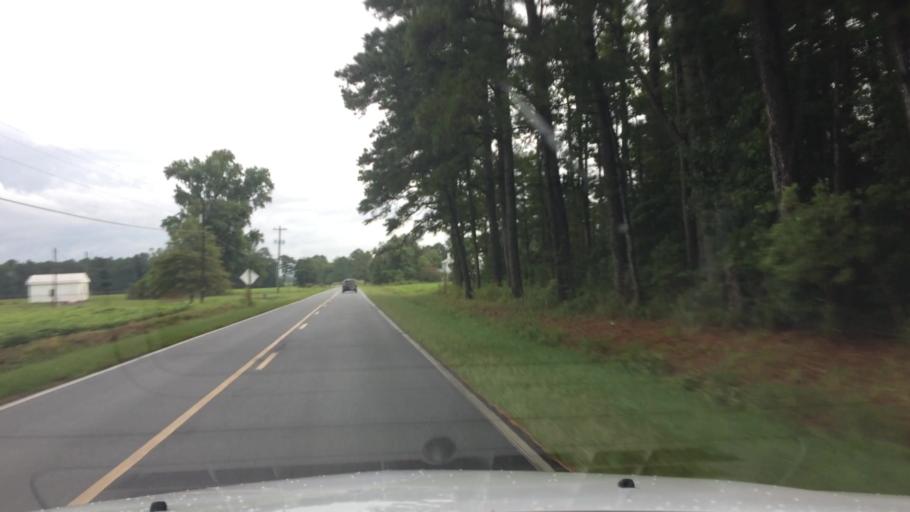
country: US
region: North Carolina
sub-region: Pitt County
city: Farmville
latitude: 35.5503
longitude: -77.5450
